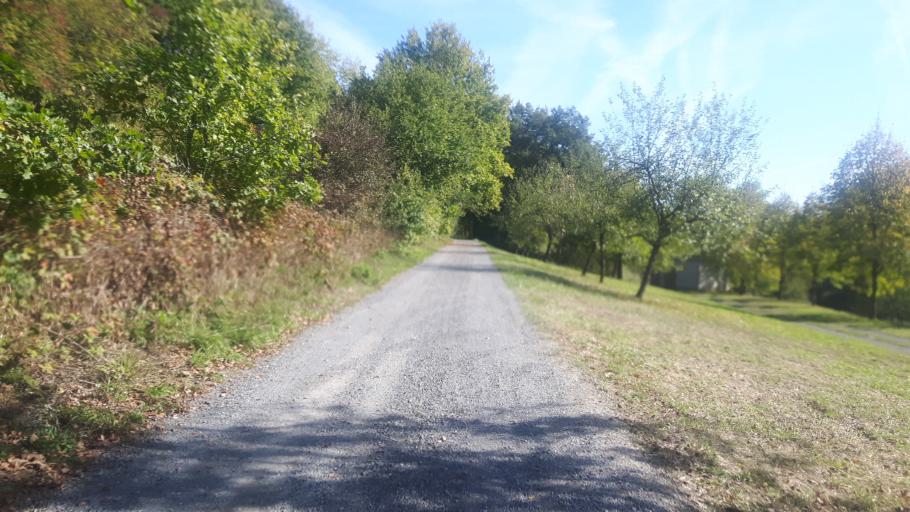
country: DE
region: Rheinland-Pfalz
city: Etzbach
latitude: 50.7767
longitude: 7.7052
